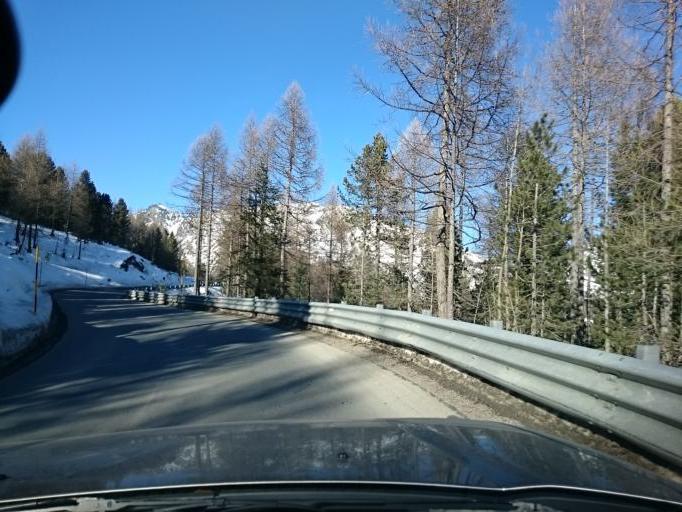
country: IT
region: Lombardy
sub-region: Provincia di Sondrio
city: Isolaccia
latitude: 46.4763
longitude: 10.2517
